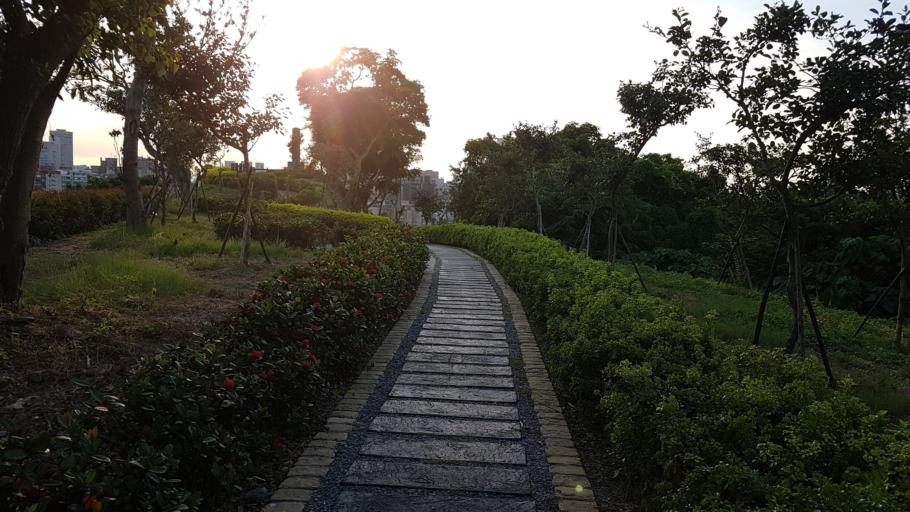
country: TW
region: Taipei
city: Taipei
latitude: 25.0220
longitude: 121.5607
